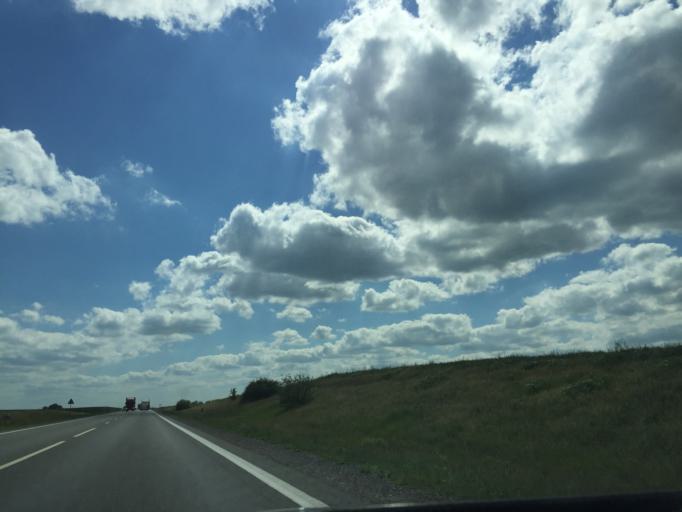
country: LT
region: Marijampoles apskritis
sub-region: Marijampole Municipality
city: Marijampole
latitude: 54.5283
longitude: 23.2475
